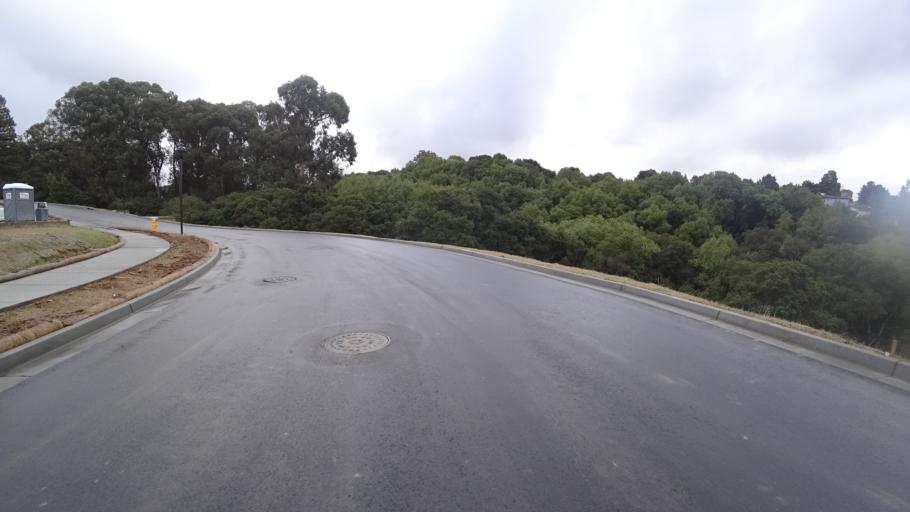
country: US
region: California
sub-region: Alameda County
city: Hayward
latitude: 37.6677
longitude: -122.0704
